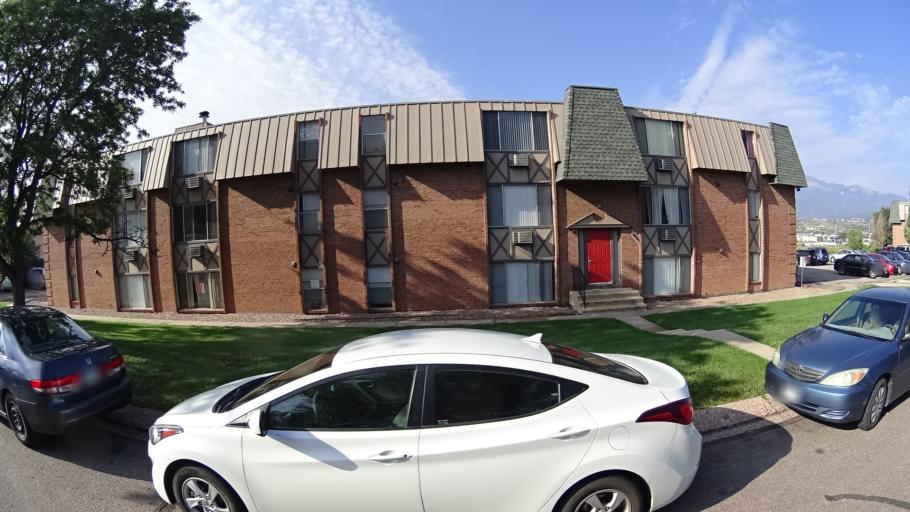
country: US
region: Colorado
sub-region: El Paso County
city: Colorado Springs
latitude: 38.8872
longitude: -104.8088
